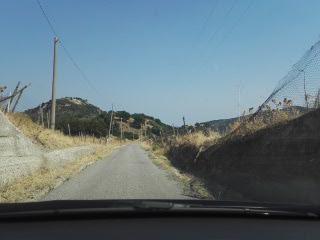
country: IT
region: Calabria
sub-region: Provincia di Reggio Calabria
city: Camini
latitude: 38.4497
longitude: 16.4637
